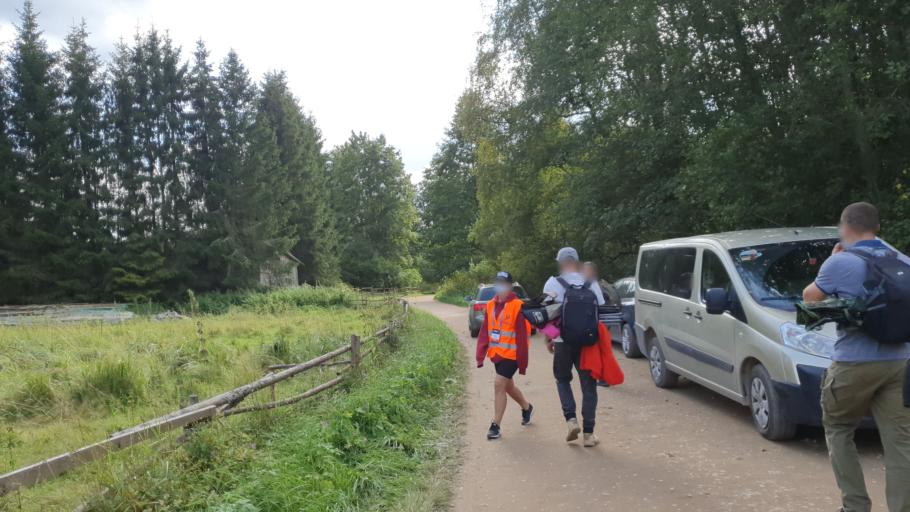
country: EE
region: Tartu
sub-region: UElenurme vald
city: Ulenurme
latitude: 58.1309
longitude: 26.7480
